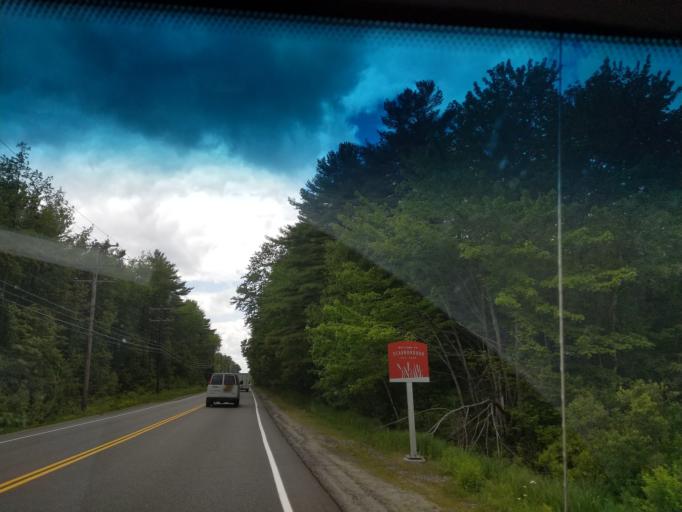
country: US
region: Maine
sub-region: Cumberland County
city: South Portland Gardens
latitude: 43.6229
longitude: -70.3324
